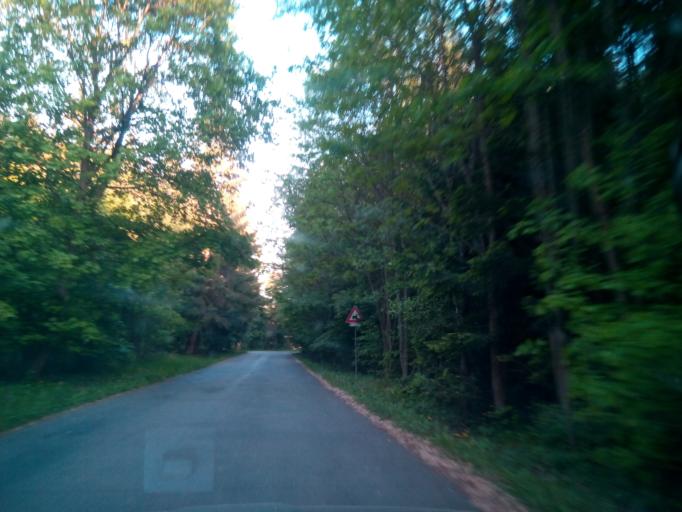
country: CZ
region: South Moravian
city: Ostrov u Macochy
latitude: 49.3711
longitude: 16.7333
